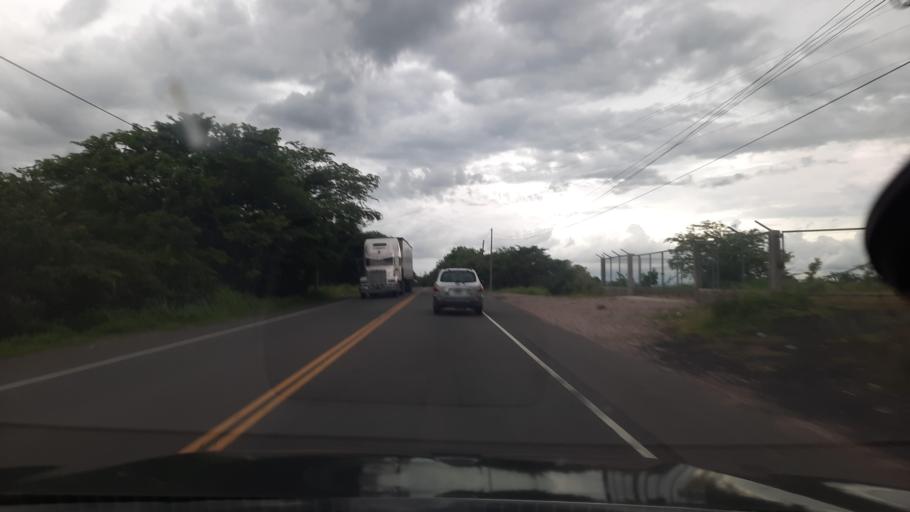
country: HN
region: Choluteca
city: Marcovia
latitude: 13.3474
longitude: -87.2588
